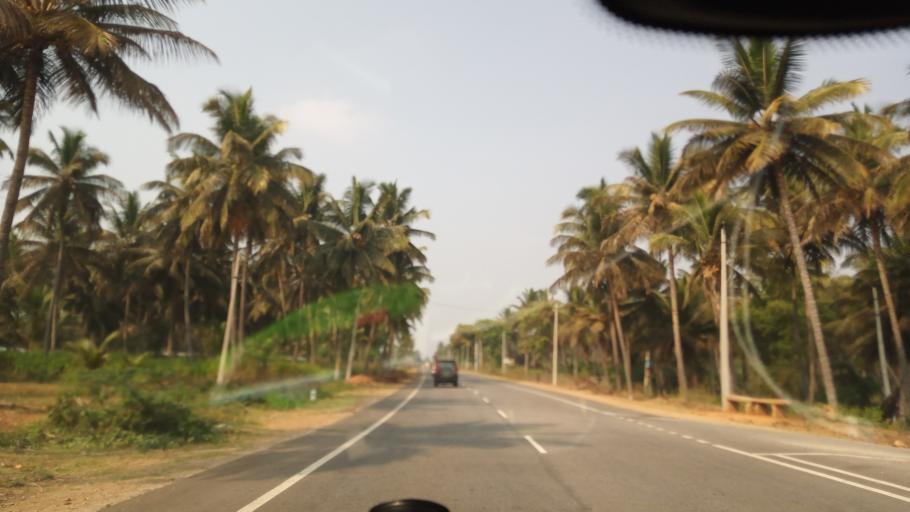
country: IN
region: Karnataka
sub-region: Mandya
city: Nagamangala
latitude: 12.7391
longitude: 76.7233
